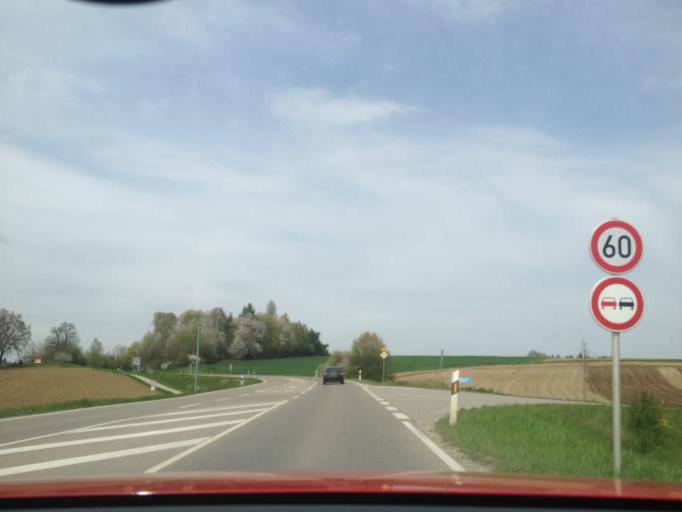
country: DE
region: Bavaria
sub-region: Upper Bavaria
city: Pfaffenhofen an der Ilm
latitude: 48.5466
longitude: 11.5114
